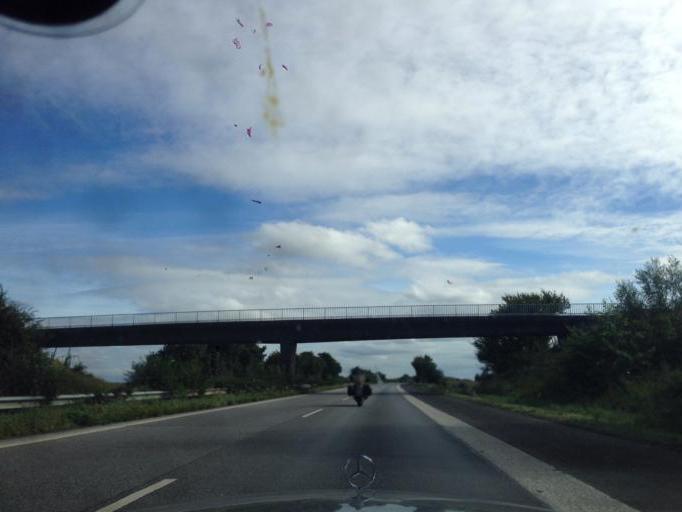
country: DE
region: Schleswig-Holstein
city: Lottorf
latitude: 54.4563
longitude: 9.5789
